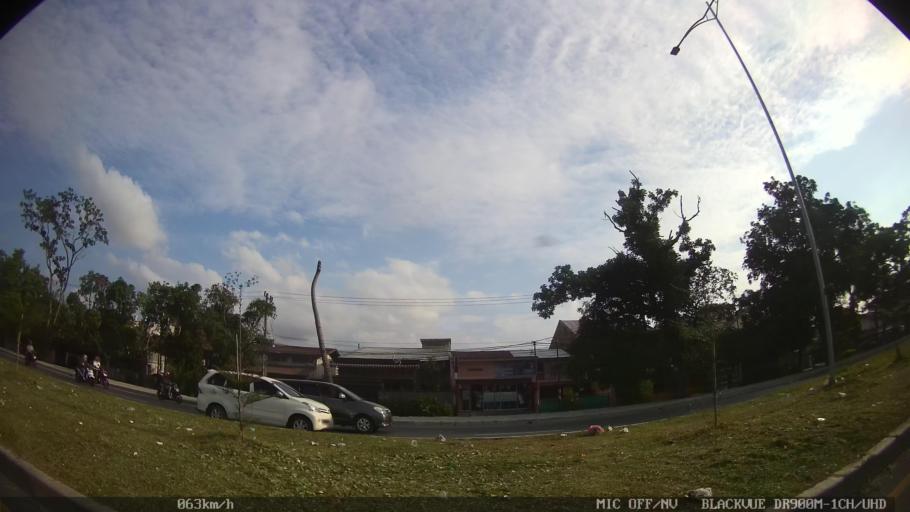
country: ID
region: North Sumatra
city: Medan
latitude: 3.6157
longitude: 98.6385
